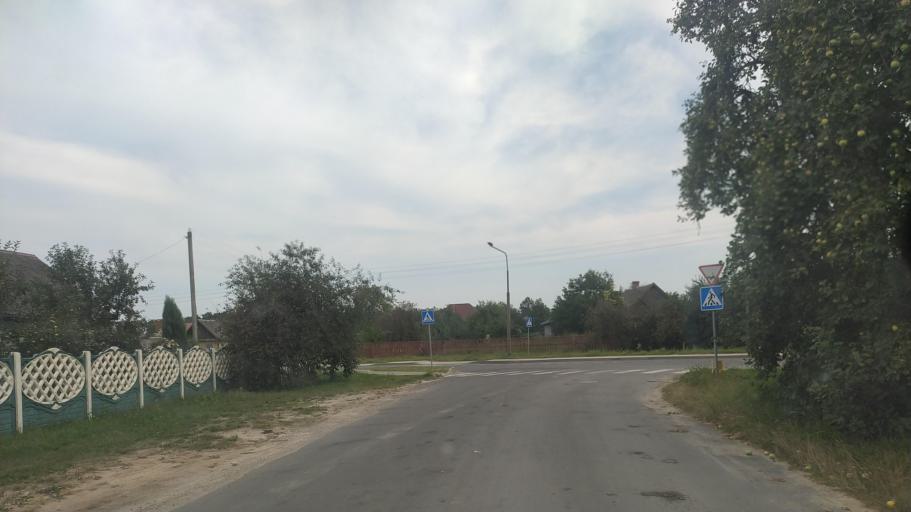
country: BY
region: Brest
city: Byaroza
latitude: 52.5428
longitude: 24.9682
